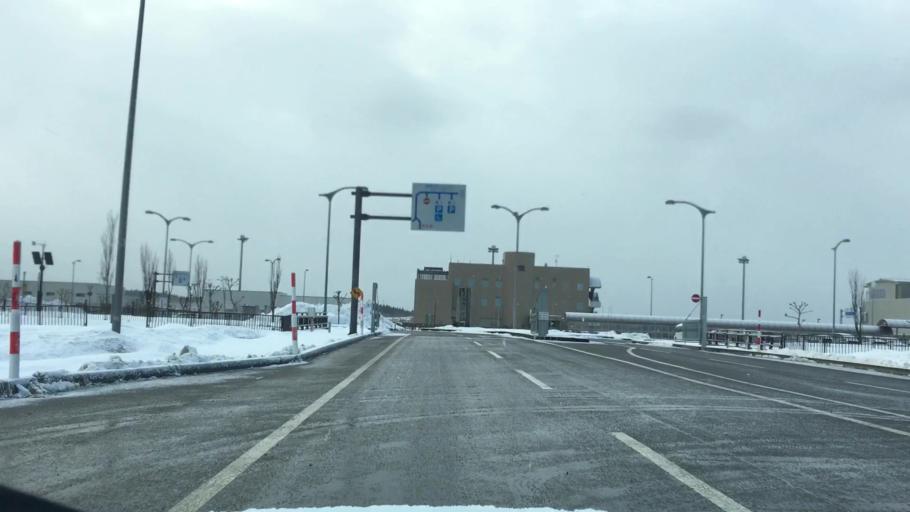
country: JP
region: Akita
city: Takanosu
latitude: 40.1970
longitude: 140.3740
